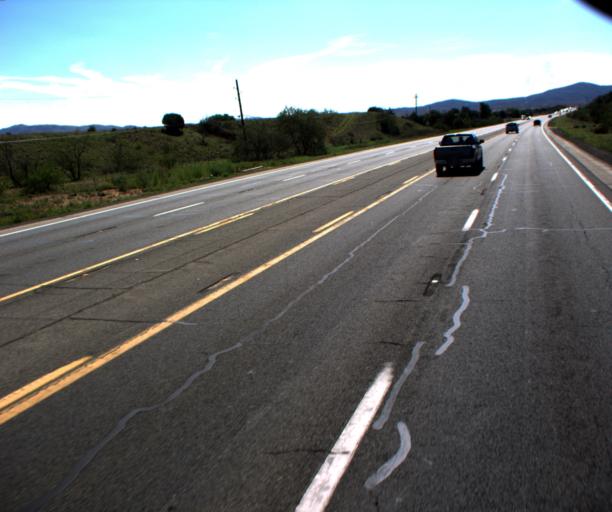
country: US
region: Arizona
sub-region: Yavapai County
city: Dewey-Humboldt
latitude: 34.5713
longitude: -112.2752
